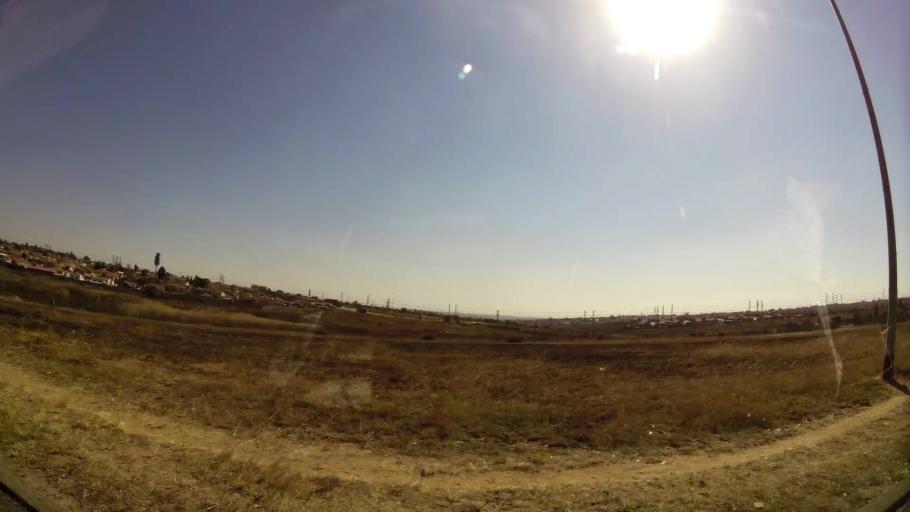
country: ZA
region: Gauteng
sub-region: Ekurhuleni Metropolitan Municipality
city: Tembisa
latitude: -26.0407
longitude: 28.2213
